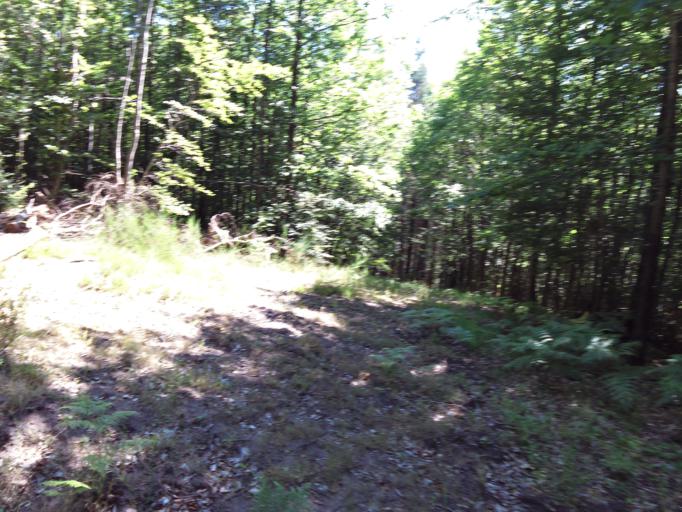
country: DE
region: Rheinland-Pfalz
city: Elmstein
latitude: 49.3911
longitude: 7.9171
